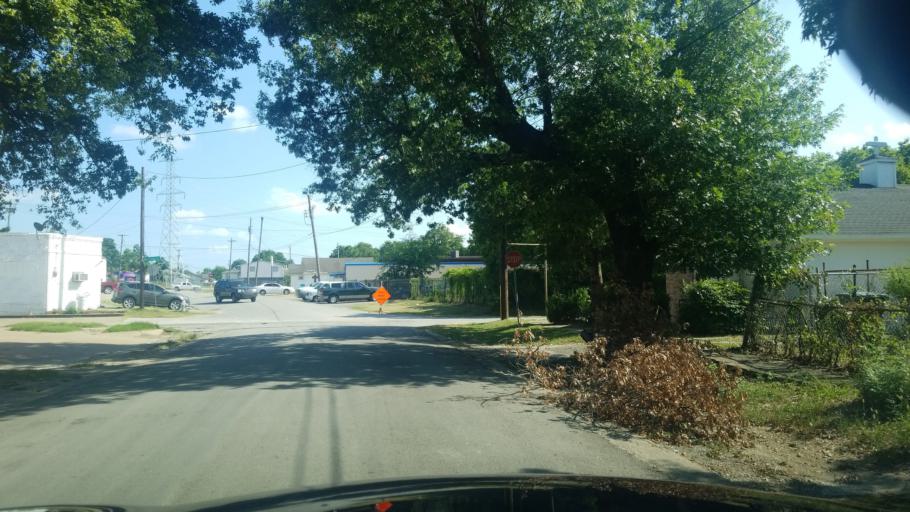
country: US
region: Texas
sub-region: Dallas County
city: Dallas
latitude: 32.7217
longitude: -96.8080
